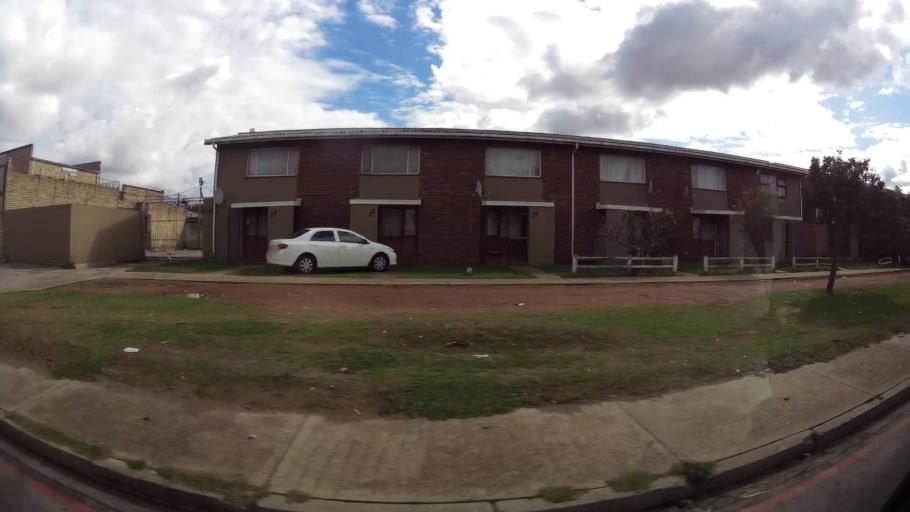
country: ZA
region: Eastern Cape
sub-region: Nelson Mandela Bay Metropolitan Municipality
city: Port Elizabeth
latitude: -33.9256
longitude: 25.5678
